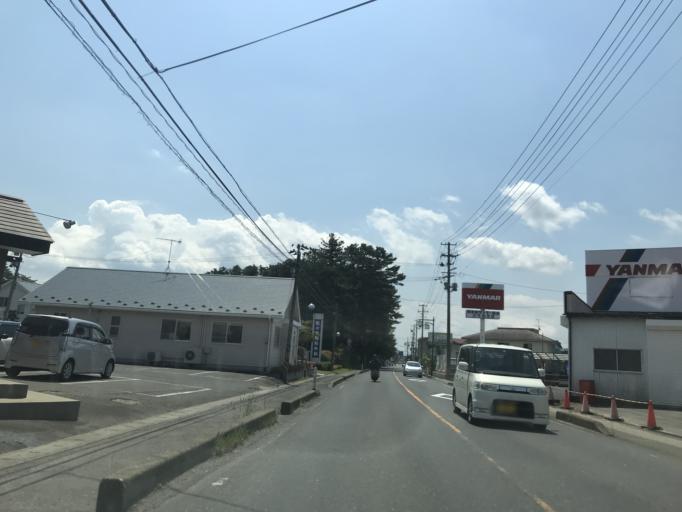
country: JP
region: Miyagi
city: Kogota
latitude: 38.5569
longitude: 141.0582
